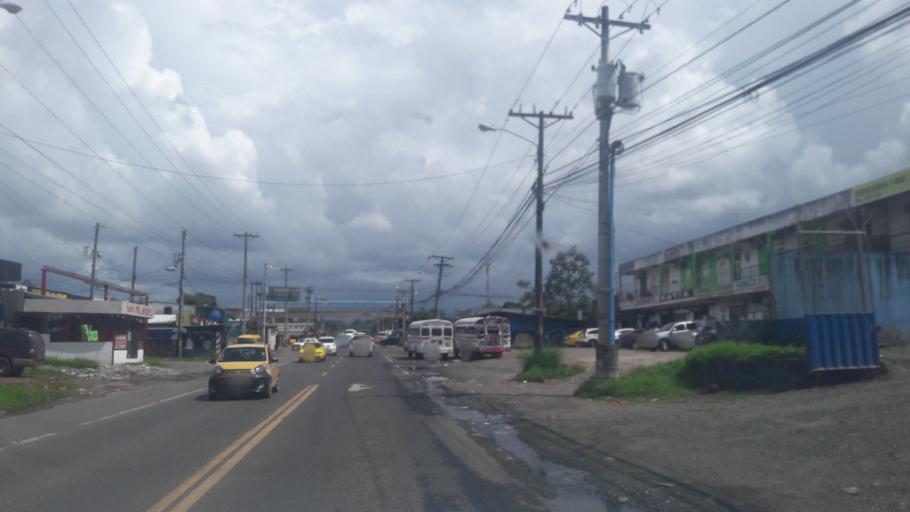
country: PA
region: Panama
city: Chilibre
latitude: 9.1225
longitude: -79.5975
